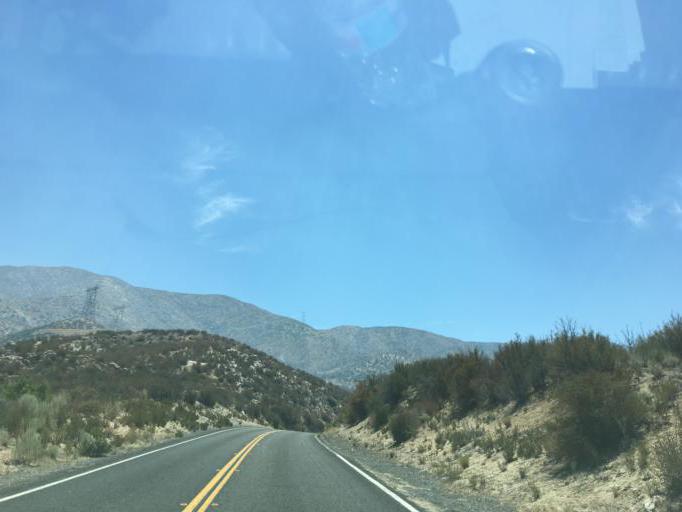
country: US
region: California
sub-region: Los Angeles County
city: Vincent
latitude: 34.4201
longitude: -118.0967
